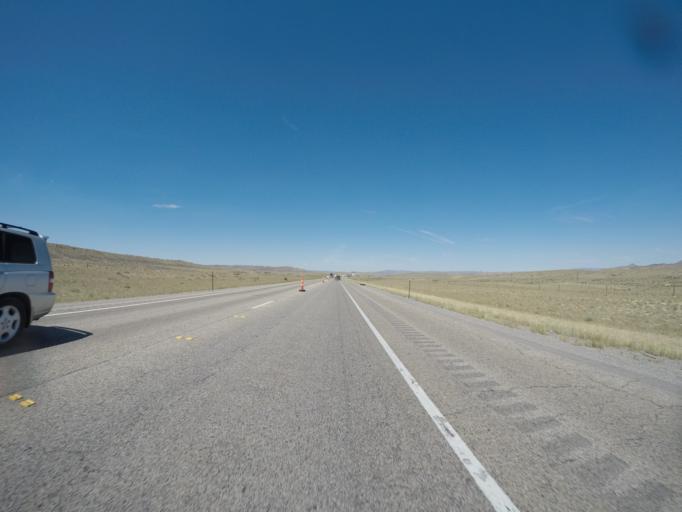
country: US
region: Wyoming
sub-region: Carbon County
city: Saratoga
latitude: 41.7447
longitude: -106.9155
